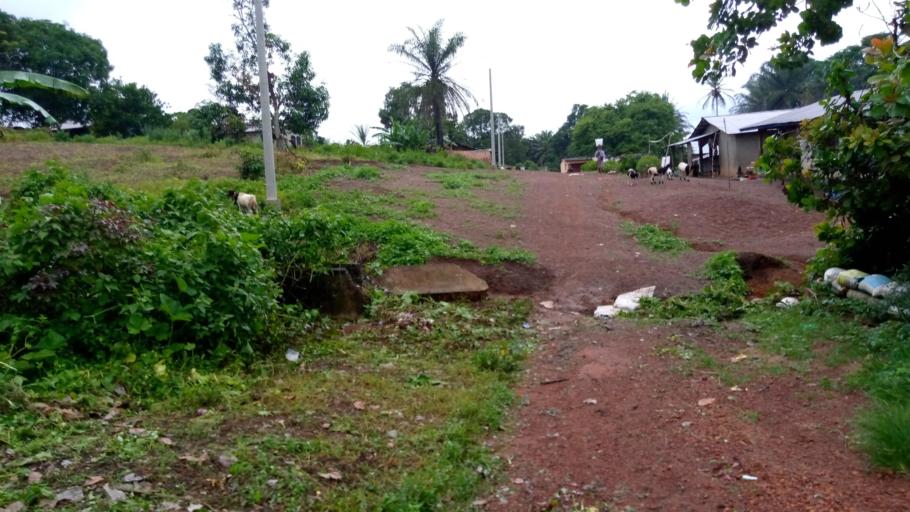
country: SL
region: Southern Province
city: Moyamba
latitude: 8.1647
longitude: -12.4380
